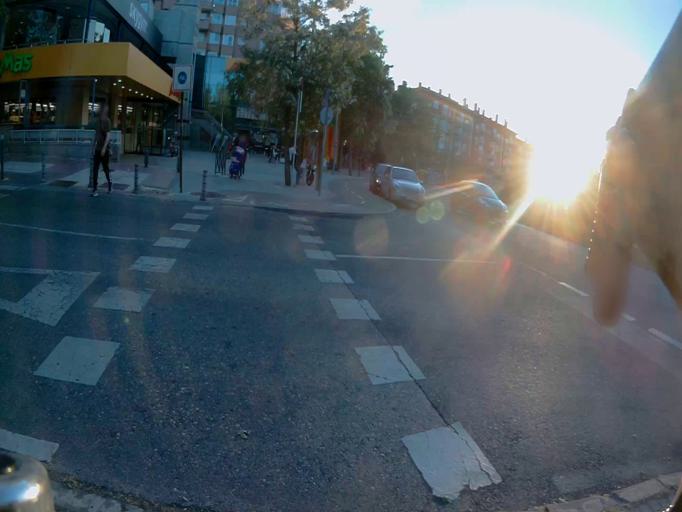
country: ES
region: Madrid
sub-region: Provincia de Madrid
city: Alcorcon
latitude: 40.3386
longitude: -3.8261
